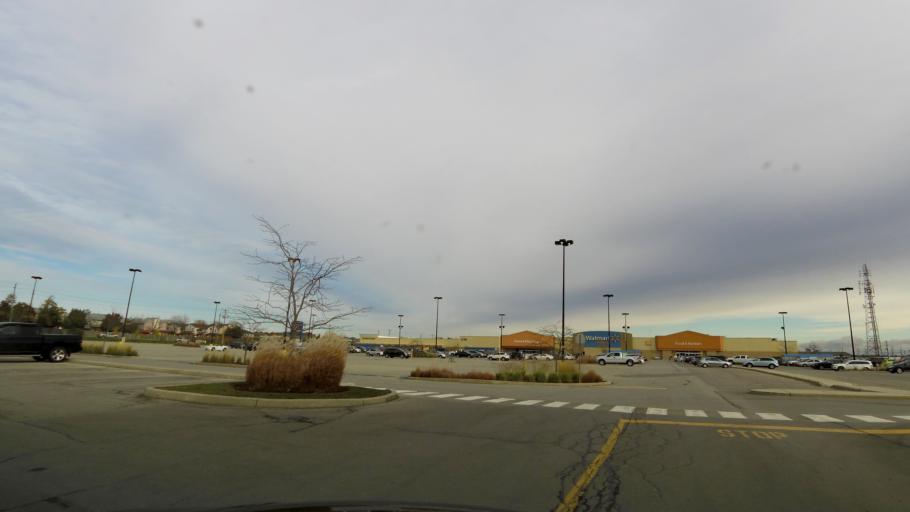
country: CA
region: Ontario
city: Hamilton
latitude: 43.1738
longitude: -79.7856
